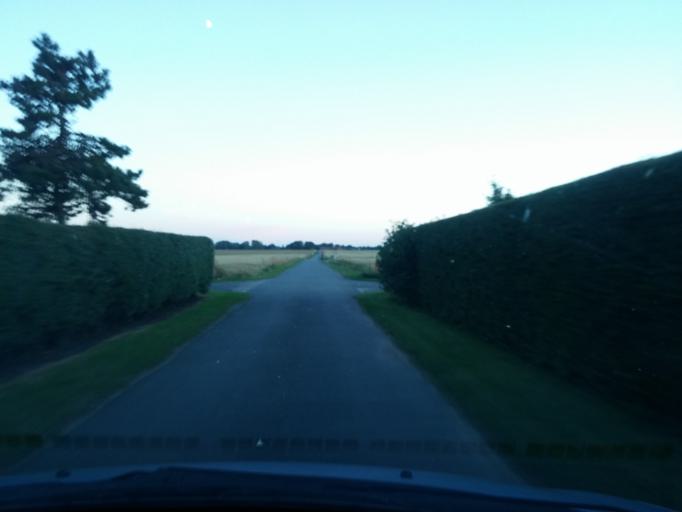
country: DK
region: South Denmark
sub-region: Nordfyns Kommune
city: Otterup
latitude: 55.5841
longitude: 10.4221
